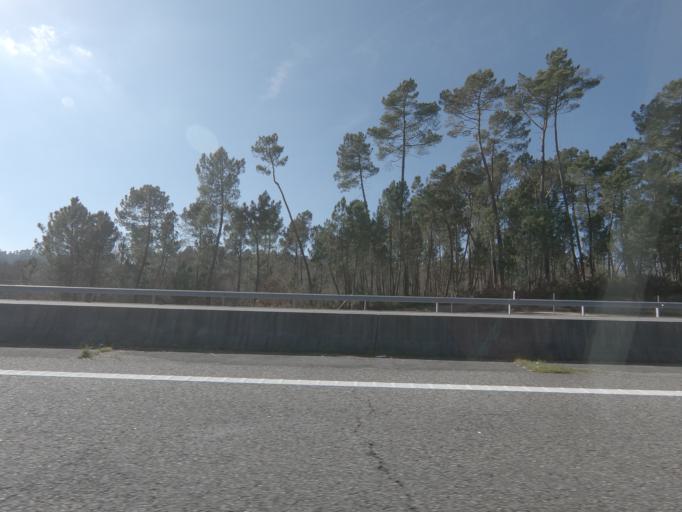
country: ES
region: Galicia
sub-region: Provincia de Ourense
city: Cea
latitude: 42.4660
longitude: -8.0273
